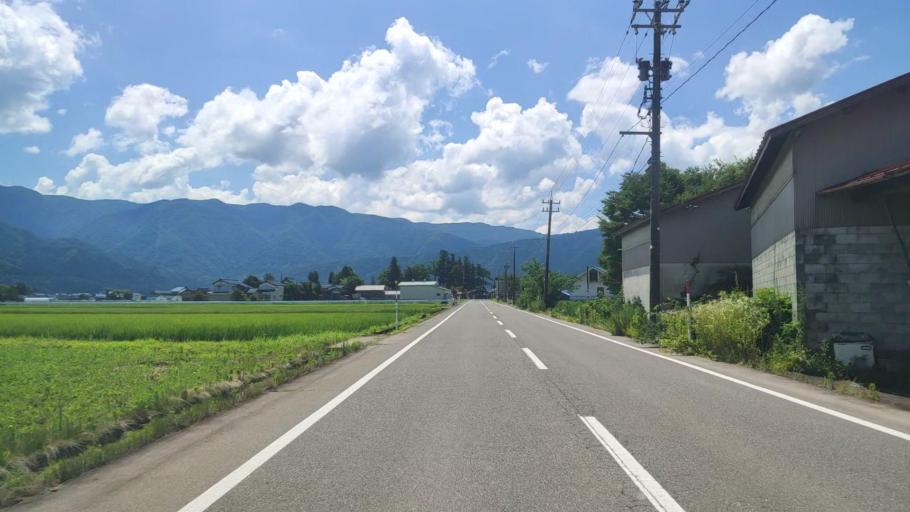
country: JP
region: Fukui
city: Ono
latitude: 35.9640
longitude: 136.5299
